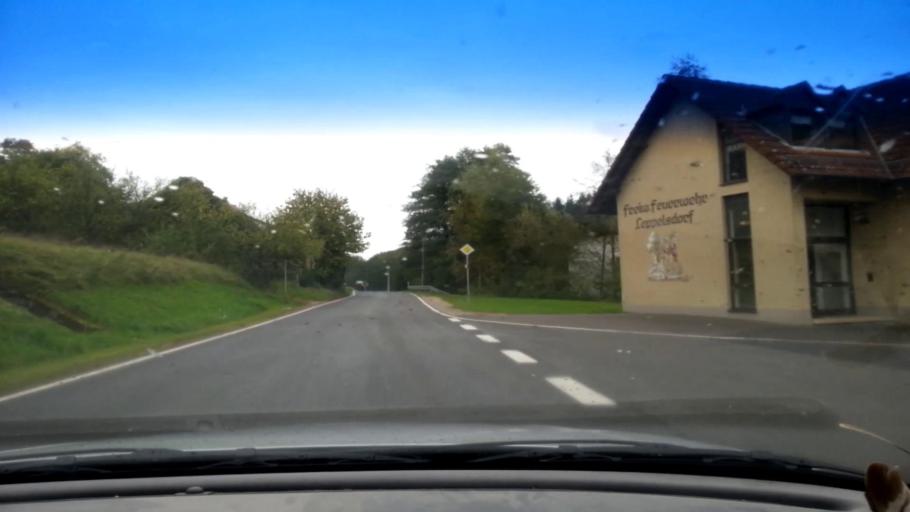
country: DE
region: Bavaria
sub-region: Upper Franconia
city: Lauter
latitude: 49.9896
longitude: 10.7585
